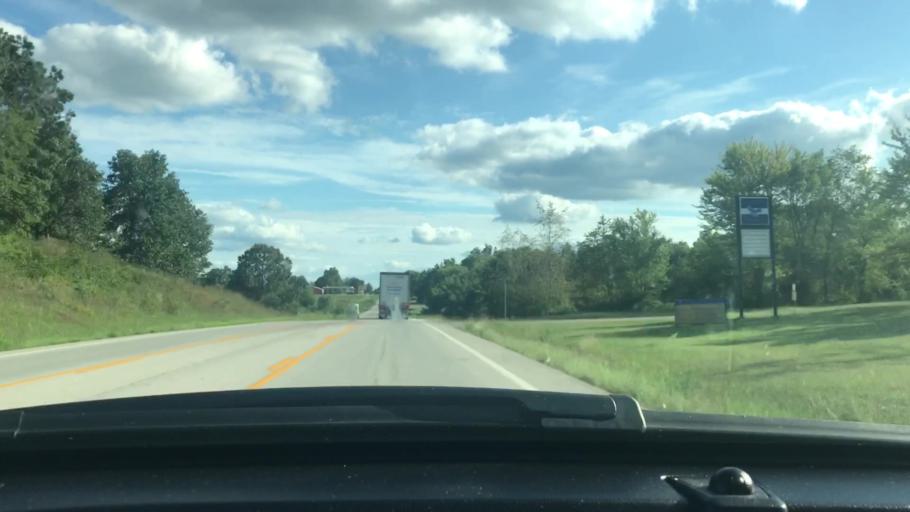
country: US
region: Missouri
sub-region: Oregon County
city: Thayer
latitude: 36.6007
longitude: -91.6440
